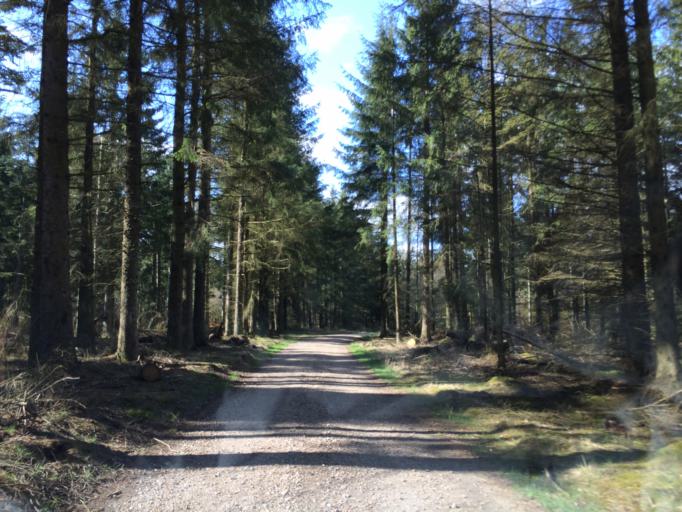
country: DK
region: Central Jutland
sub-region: Holstebro Kommune
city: Ulfborg
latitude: 56.2227
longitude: 8.4641
